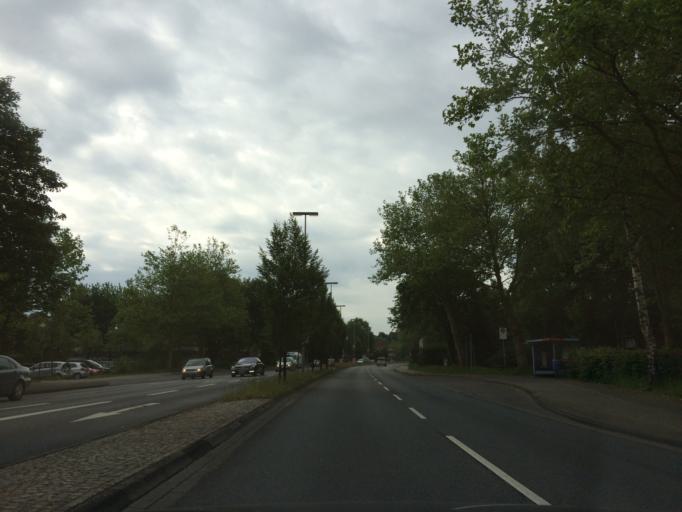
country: DE
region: Lower Saxony
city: Delmenhorst
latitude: 53.0497
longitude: 8.6341
